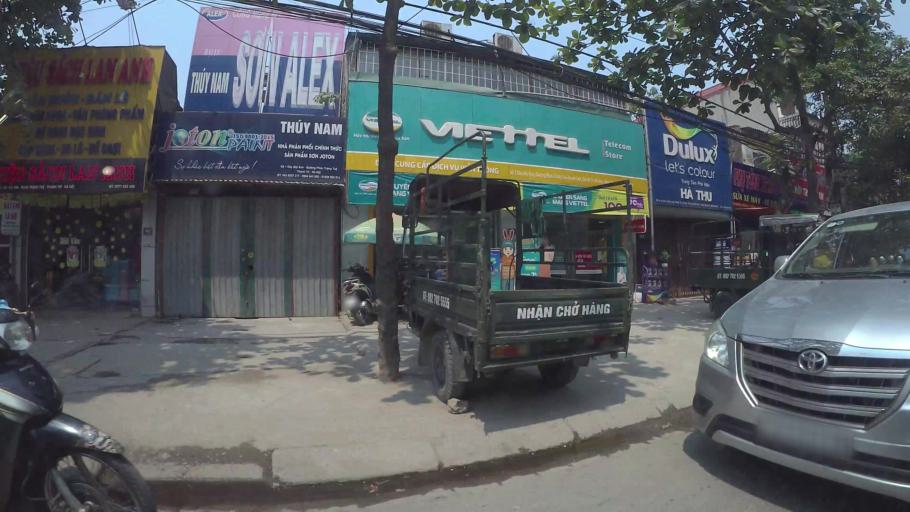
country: VN
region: Ha Noi
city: Van Dien
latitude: 20.9557
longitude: 105.8108
